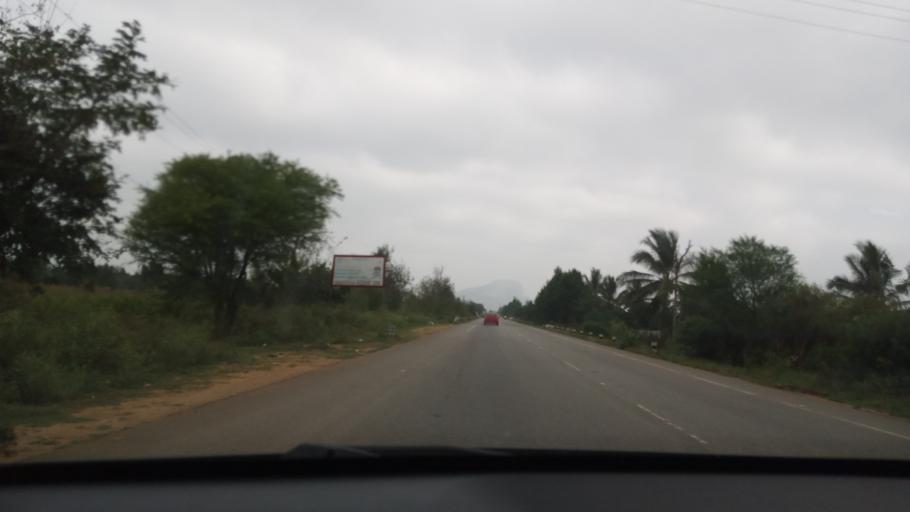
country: IN
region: Karnataka
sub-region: Chikkaballapur
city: Chintamani
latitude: 13.2981
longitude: 77.9689
